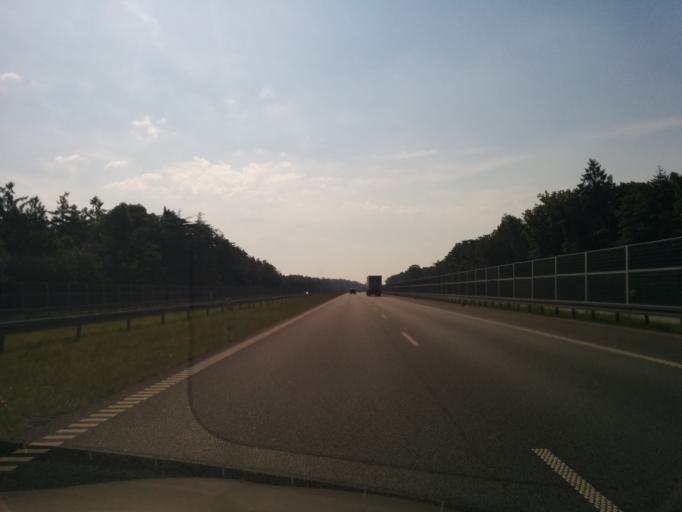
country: PL
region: Silesian Voivodeship
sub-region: Powiat tarnogorski
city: Radzionkow
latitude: 50.3842
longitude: 18.8565
